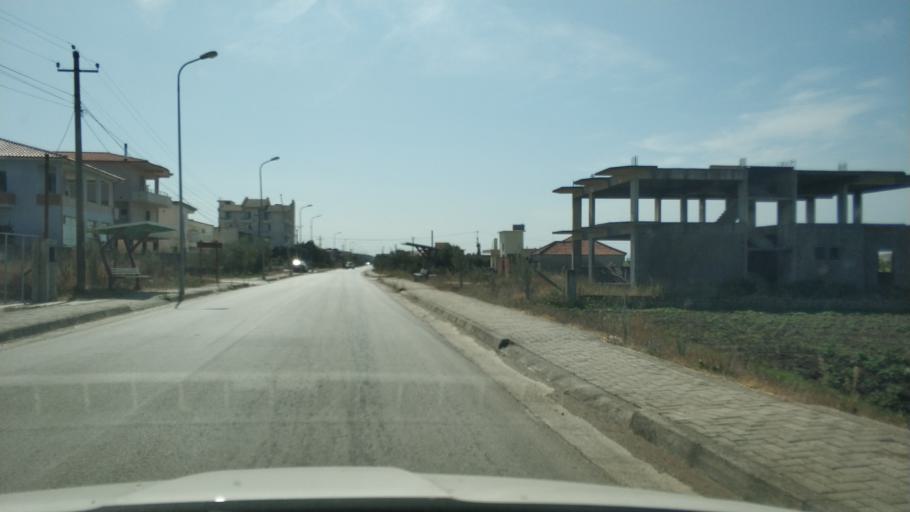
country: AL
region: Fier
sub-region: Rrethi i Lushnjes
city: Divjake
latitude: 40.9754
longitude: 19.5356
